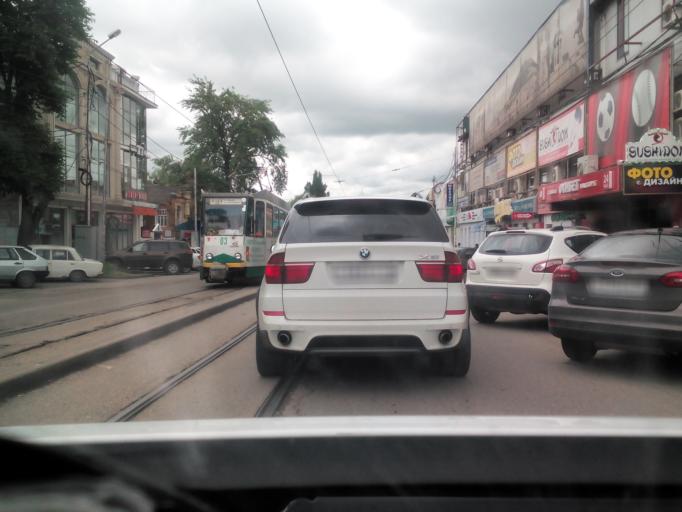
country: RU
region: Stavropol'skiy
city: Pyatigorsk
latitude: 44.0420
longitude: 43.0642
